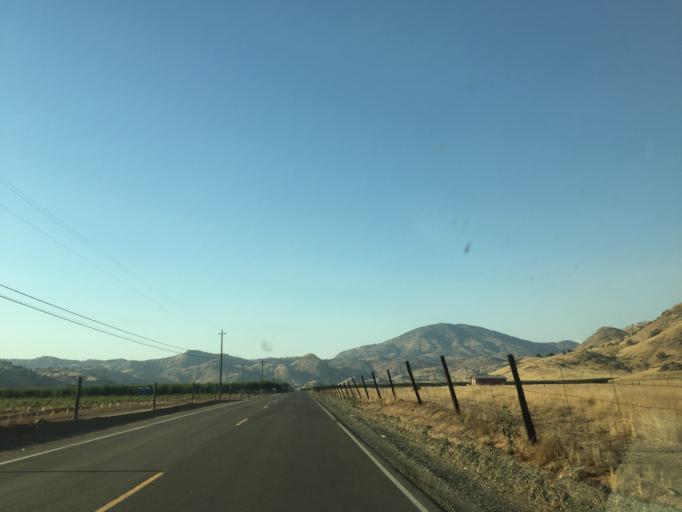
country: US
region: California
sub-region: Fresno County
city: Orange Cove
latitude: 36.6768
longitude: -119.3045
